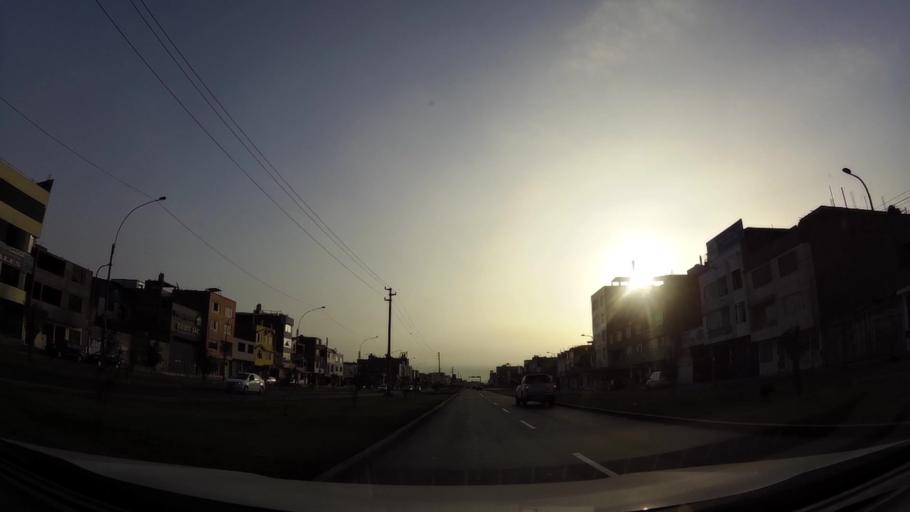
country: PE
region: Lima
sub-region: Lima
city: Independencia
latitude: -11.9911
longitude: -77.0866
